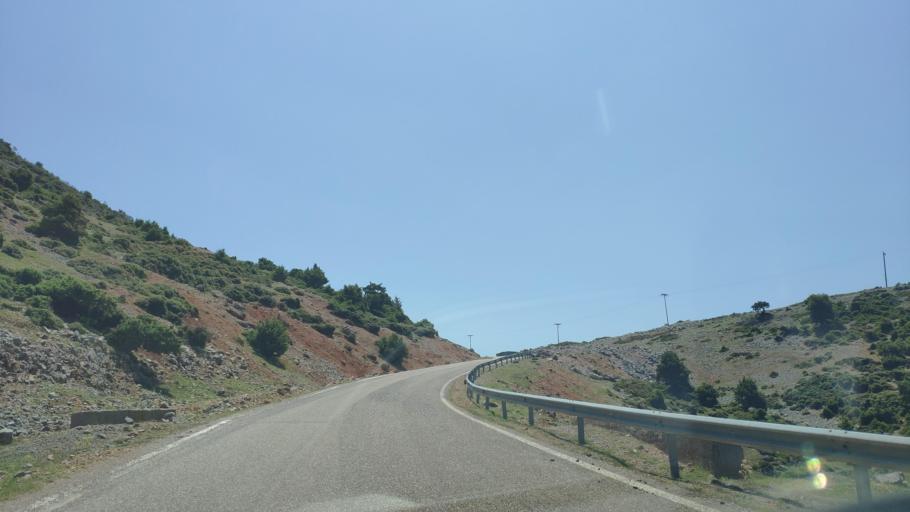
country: GR
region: West Greece
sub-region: Nomos Aitolias kai Akarnanias
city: Krikellos
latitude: 39.0520
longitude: 21.3712
